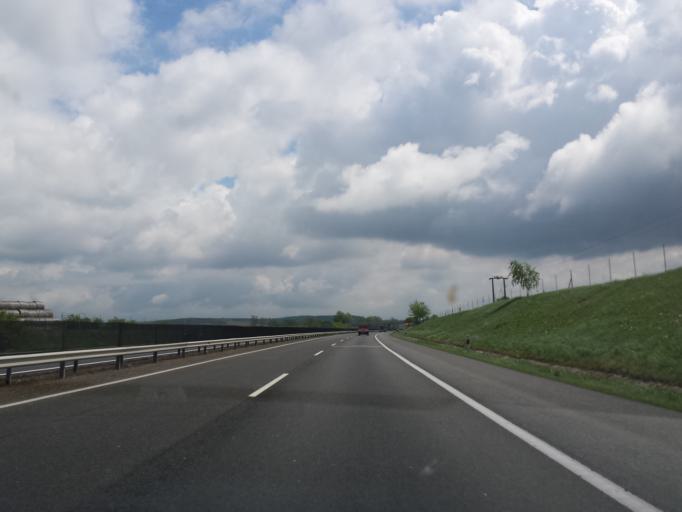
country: HU
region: Komarom-Esztergom
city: Mocsa
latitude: 47.6593
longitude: 18.1827
